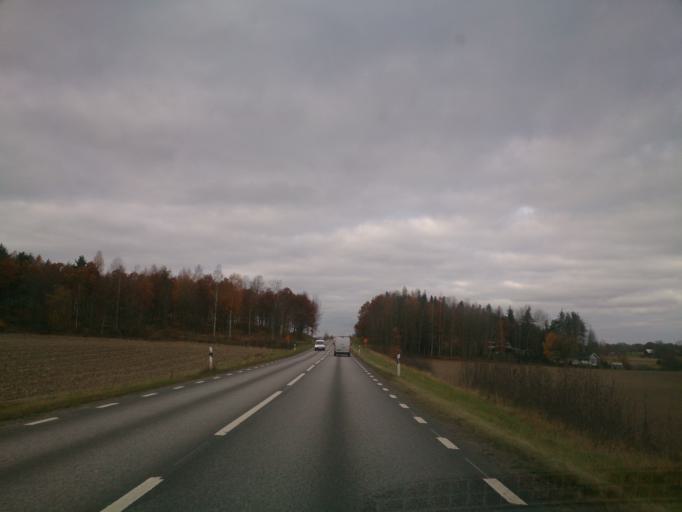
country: SE
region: OEstergoetland
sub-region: Linkopings Kommun
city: Linghem
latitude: 58.3776
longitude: 15.8032
